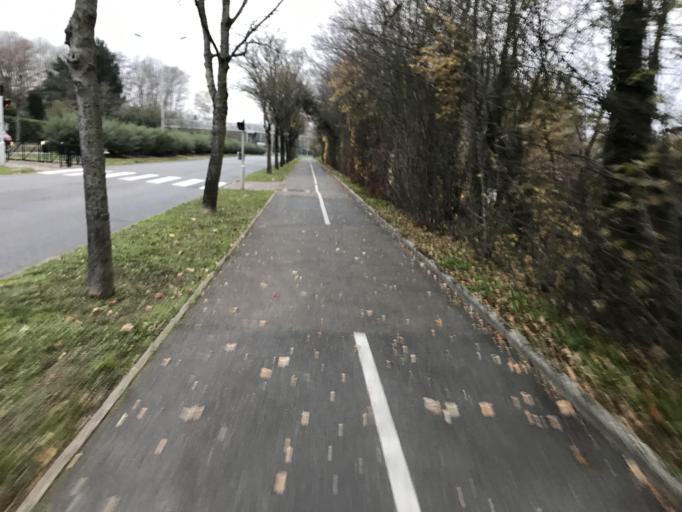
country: FR
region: Ile-de-France
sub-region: Departement des Yvelines
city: Montigny-le-Bretonneux
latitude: 48.7662
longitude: 2.0293
